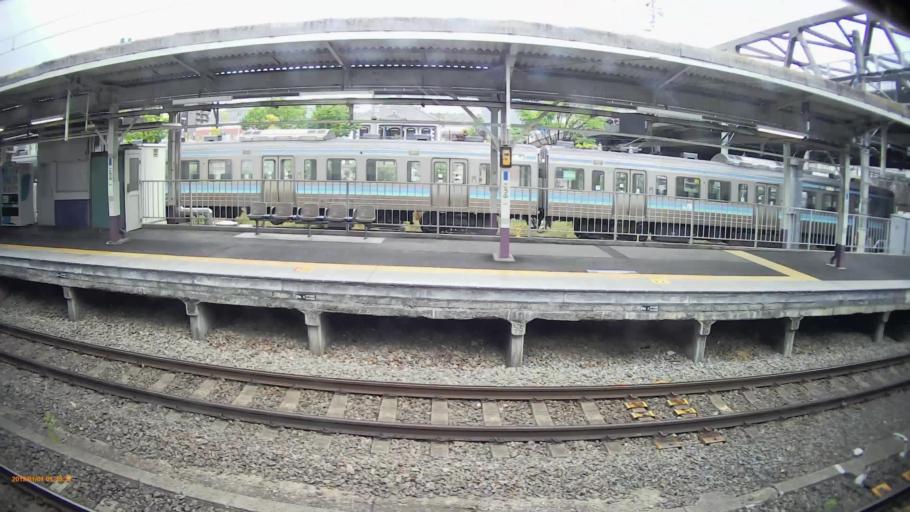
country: JP
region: Yamanashi
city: Kofu-shi
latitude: 35.6671
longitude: 138.5699
